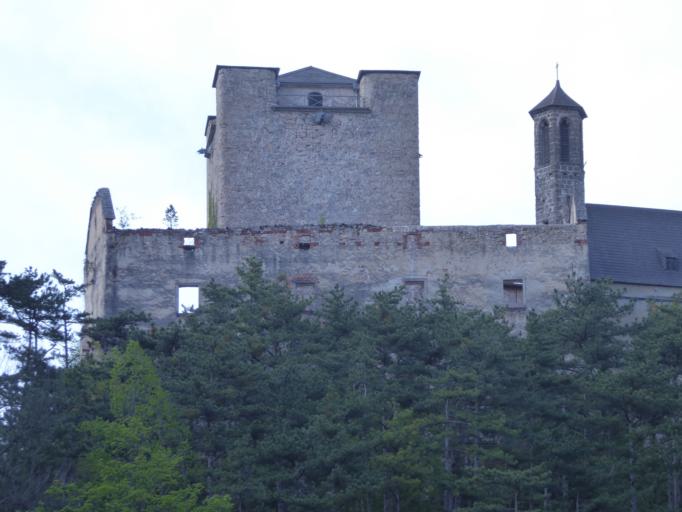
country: AT
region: Lower Austria
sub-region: Politischer Bezirk Neunkirchen
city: Schrattenbach
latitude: 47.7430
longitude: 15.9790
